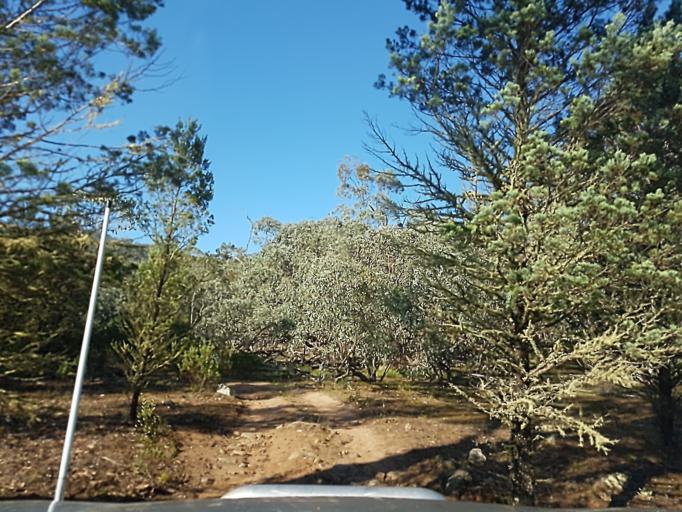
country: AU
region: New South Wales
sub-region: Snowy River
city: Jindabyne
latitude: -36.9442
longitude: 148.3835
